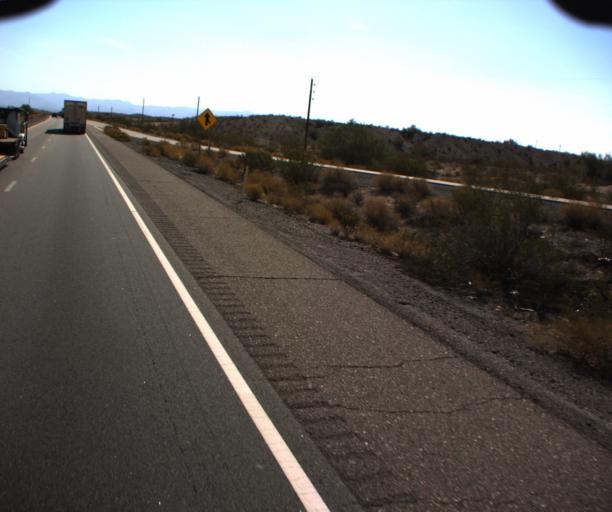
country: US
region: Arizona
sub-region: Mohave County
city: Desert Hills
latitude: 34.7346
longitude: -114.2566
